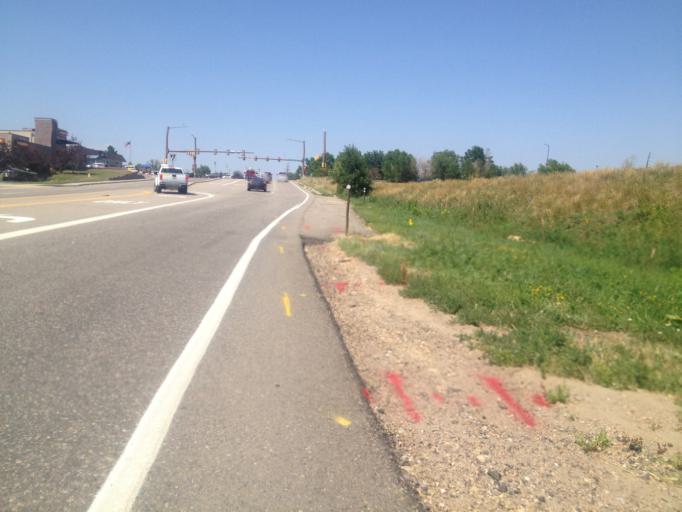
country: US
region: Colorado
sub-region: Boulder County
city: Louisville
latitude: 39.9853
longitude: -105.1278
